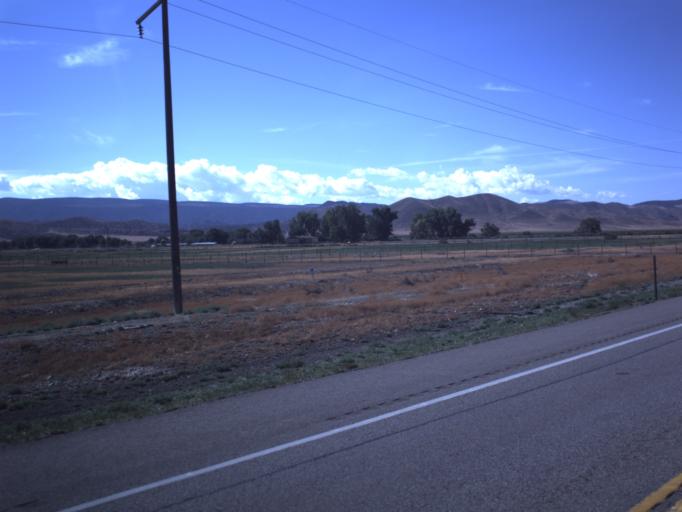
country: US
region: Utah
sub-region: Sanpete County
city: Centerfield
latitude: 39.0507
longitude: -111.8234
